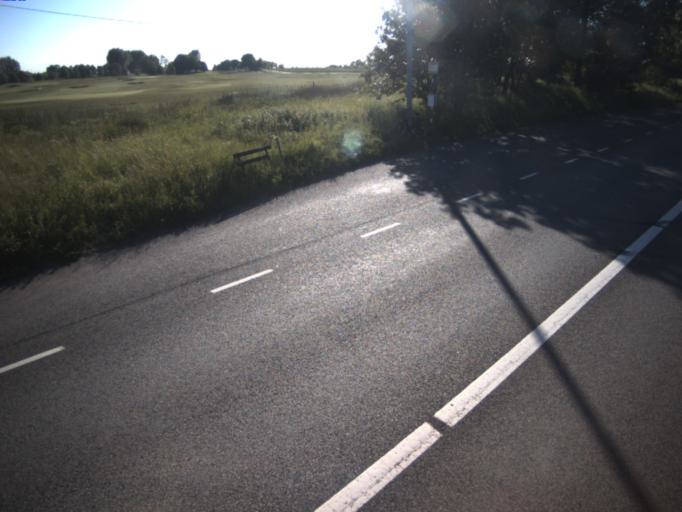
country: SE
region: Skane
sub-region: Helsingborg
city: Rydeback
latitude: 55.9772
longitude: 12.7736
